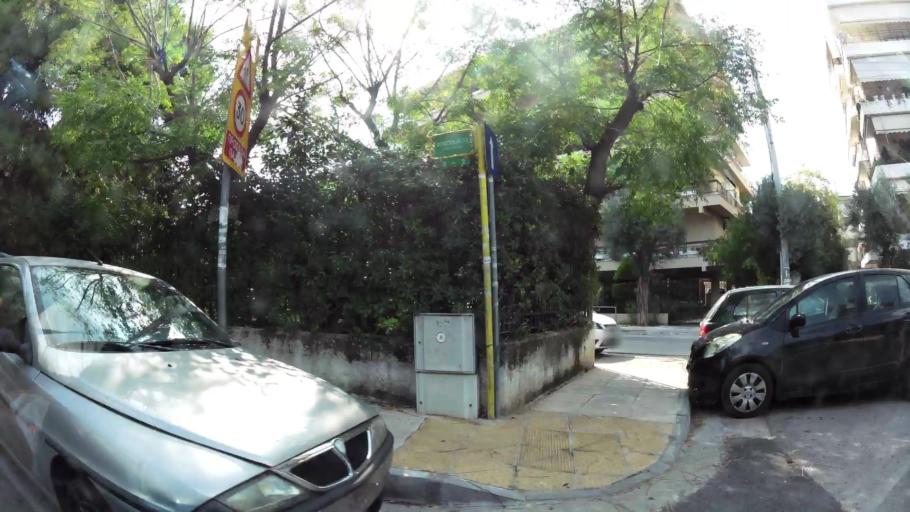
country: GR
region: Attica
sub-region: Nomarchia Athinas
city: Cholargos
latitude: 38.0026
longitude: 23.7999
